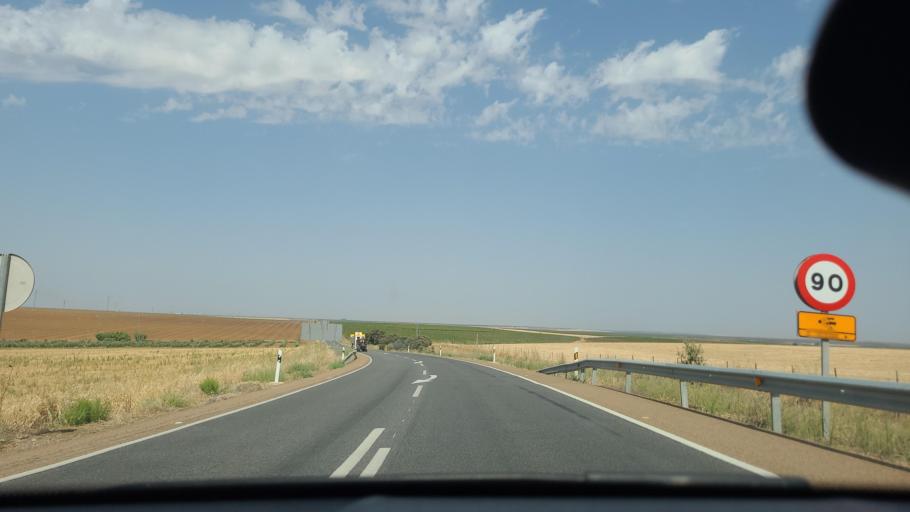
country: ES
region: Extremadura
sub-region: Provincia de Badajoz
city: Santa Marta
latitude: 38.6261
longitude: -6.6634
